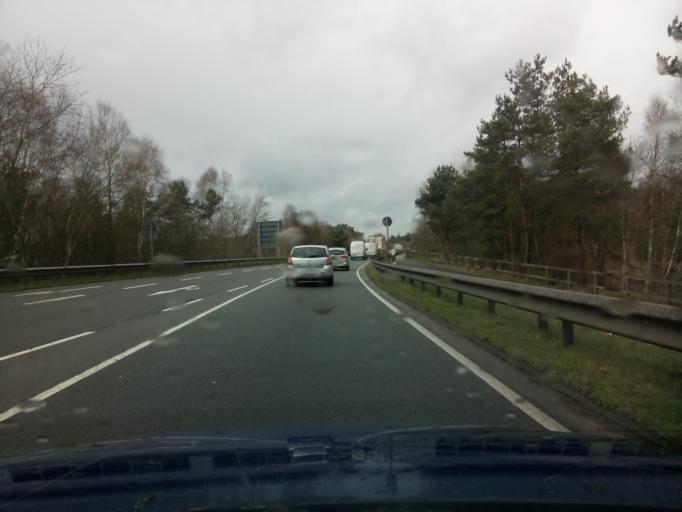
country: DE
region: Lower Saxony
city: Meppen
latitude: 52.7064
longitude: 7.3162
